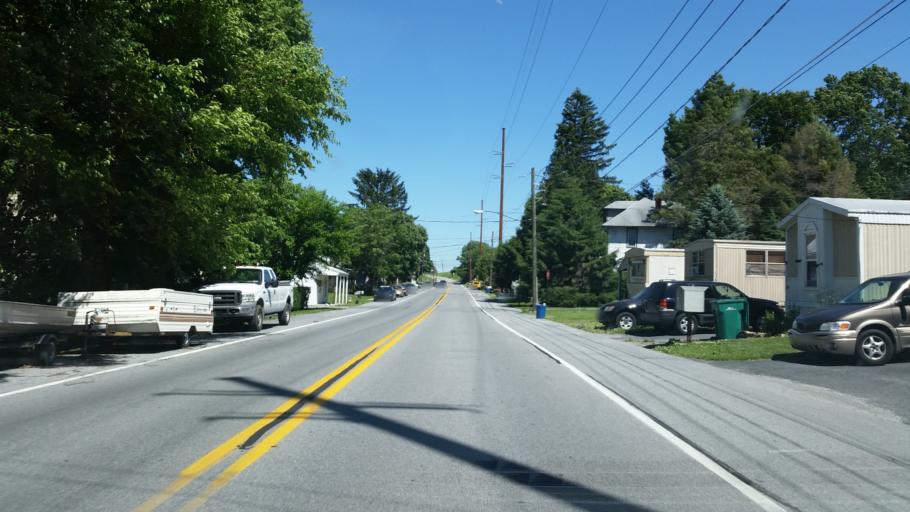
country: US
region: Pennsylvania
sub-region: Dauphin County
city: Steelton
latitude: 40.2229
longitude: -76.8528
